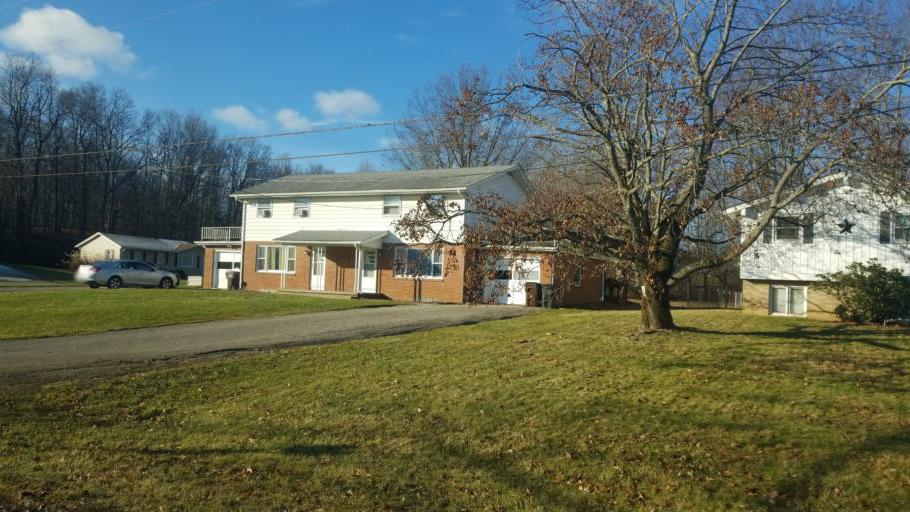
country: US
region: Ohio
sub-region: Richland County
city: Ontario
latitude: 40.7576
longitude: -82.5940
